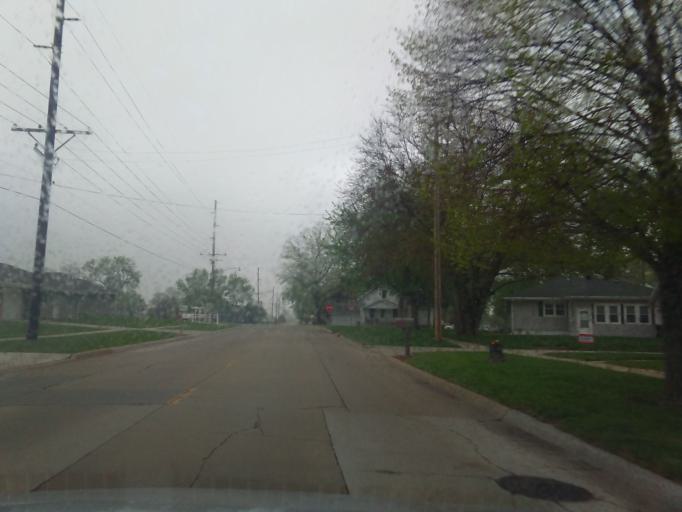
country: US
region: Nebraska
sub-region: Madison County
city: Norfolk
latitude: 42.0428
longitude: -97.4194
